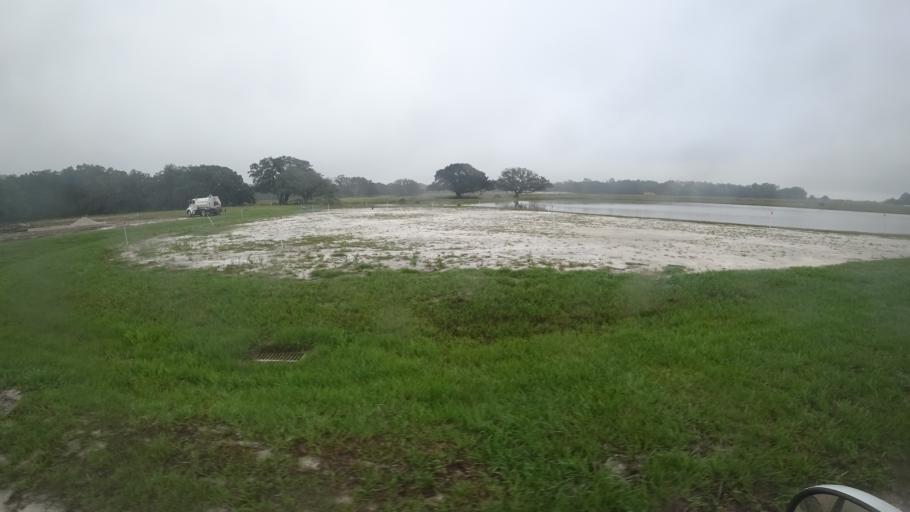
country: US
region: Florida
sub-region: Sarasota County
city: Lake Sarasota
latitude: 27.2924
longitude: -82.2191
